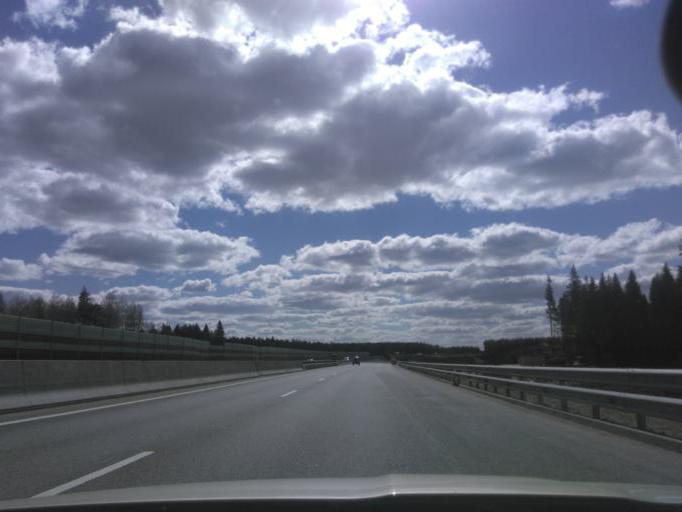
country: RU
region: Moskovskaya
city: Radumlya
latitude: 56.0903
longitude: 37.1992
